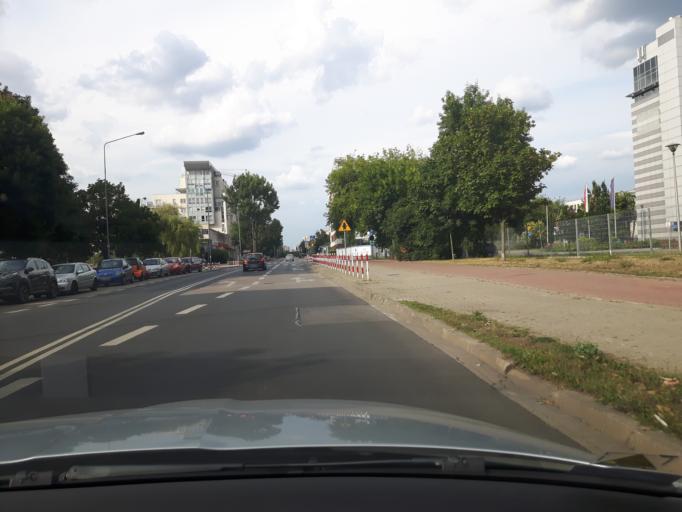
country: PL
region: Masovian Voivodeship
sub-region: Warszawa
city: Mokotow
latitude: 52.1703
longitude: 21.0104
